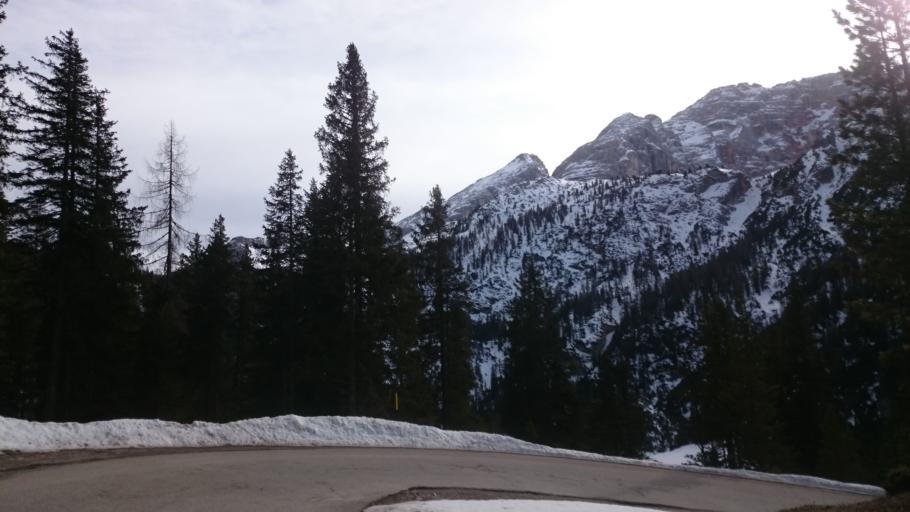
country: IT
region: Trentino-Alto Adige
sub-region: Bolzano
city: Braies
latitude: 46.6598
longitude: 12.1681
